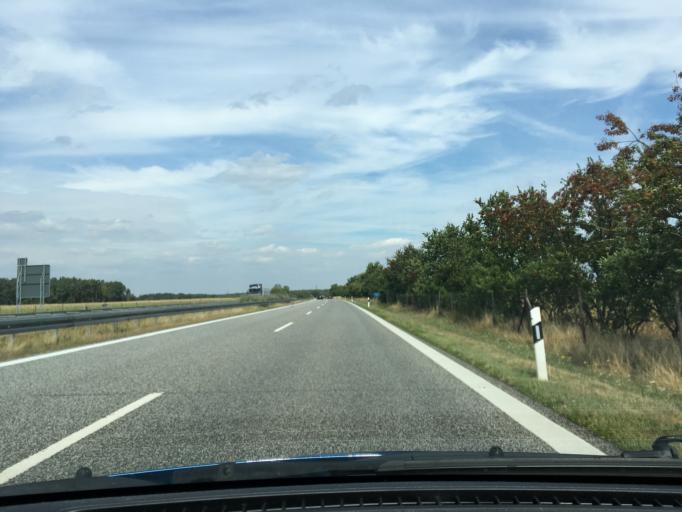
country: DE
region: Mecklenburg-Vorpommern
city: Plate
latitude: 53.5403
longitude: 11.4708
